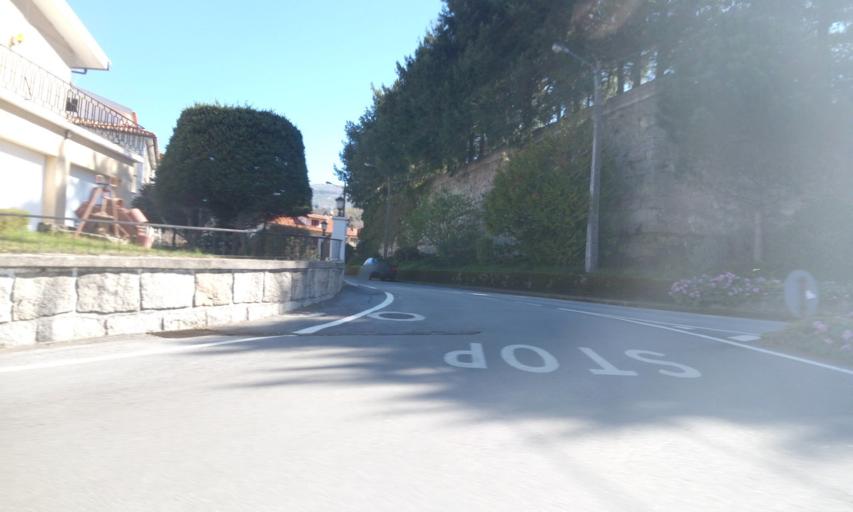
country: PT
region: Guarda
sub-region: Manteigas
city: Manteigas
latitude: 40.4866
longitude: -7.5950
